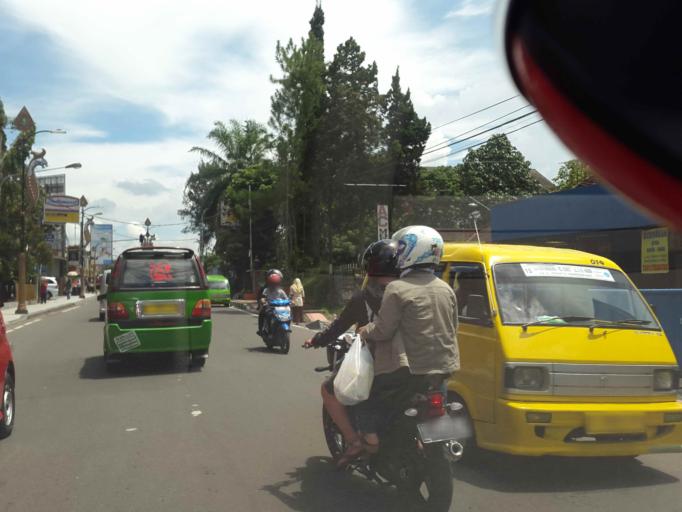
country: ID
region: West Java
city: Sukabumi
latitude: -6.9204
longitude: 106.9301
